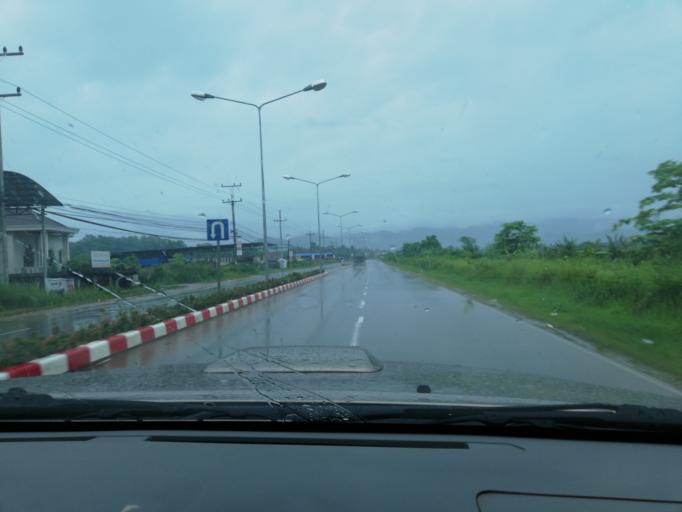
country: LA
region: Loungnamtha
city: Louang Namtha
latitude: 20.9594
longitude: 101.4040
